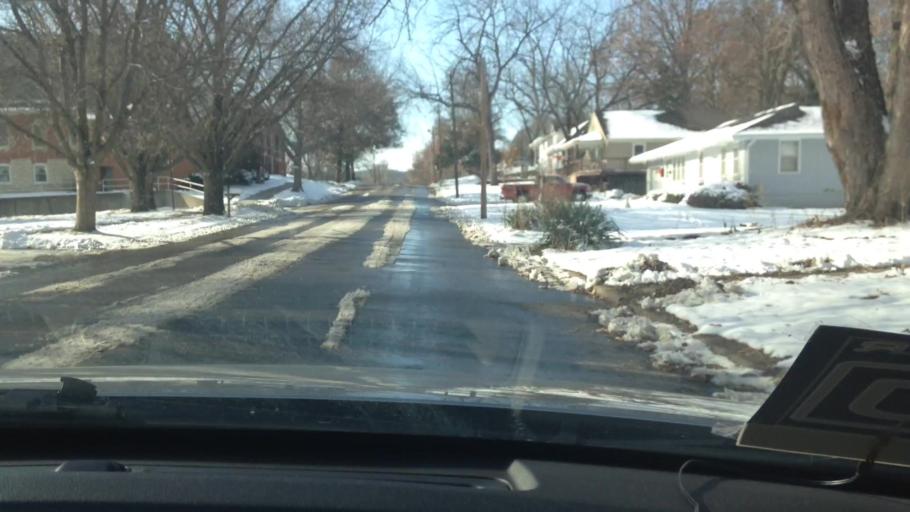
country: US
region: Kansas
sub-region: Leavenworth County
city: Leavenworth
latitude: 39.3008
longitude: -94.9187
